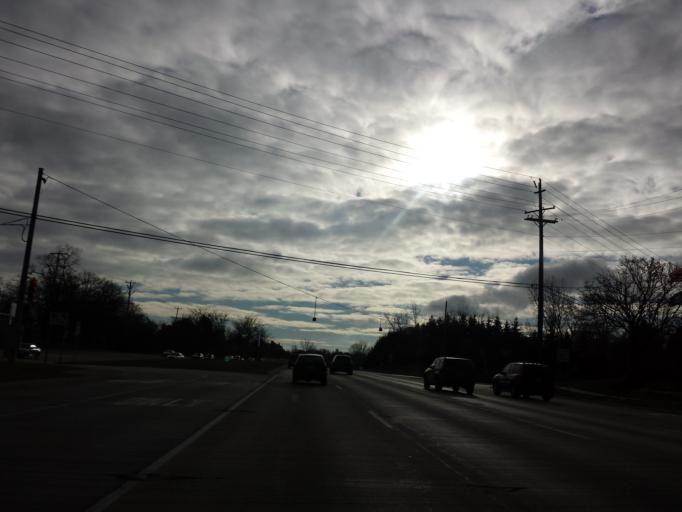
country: US
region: Michigan
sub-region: Oakland County
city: Pontiac
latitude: 42.6017
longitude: -83.2878
